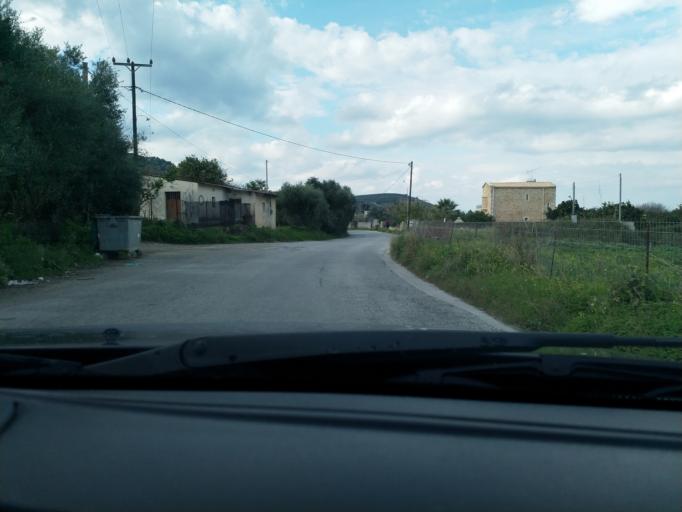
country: GR
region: Crete
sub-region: Nomos Chanias
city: Agia Marina
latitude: 35.4982
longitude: 23.9023
